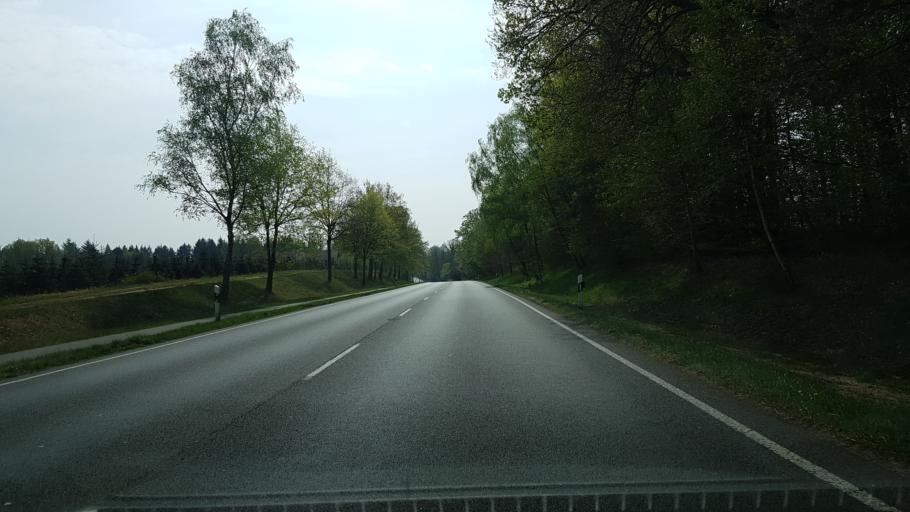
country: DE
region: Lower Saxony
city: Soltau
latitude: 52.9600
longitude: 9.8605
